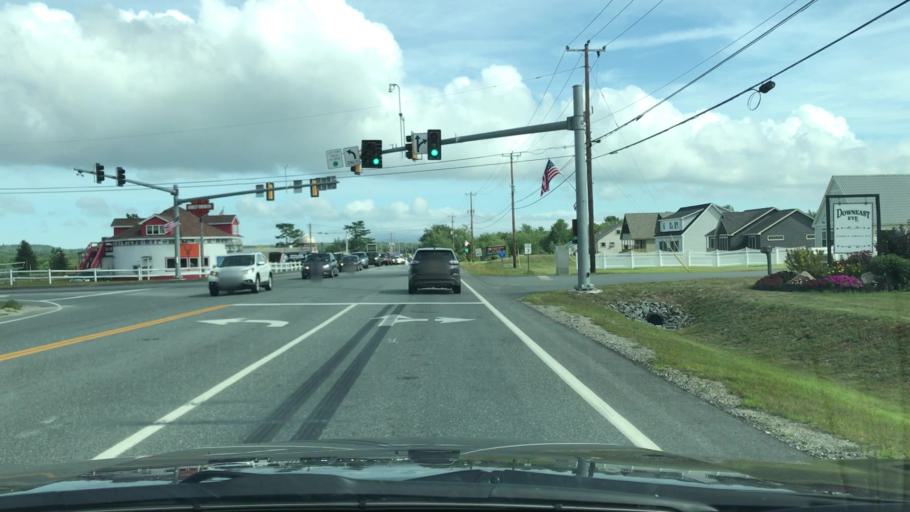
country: US
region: Maine
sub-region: Hancock County
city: Trenton
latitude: 44.4888
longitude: -68.3712
